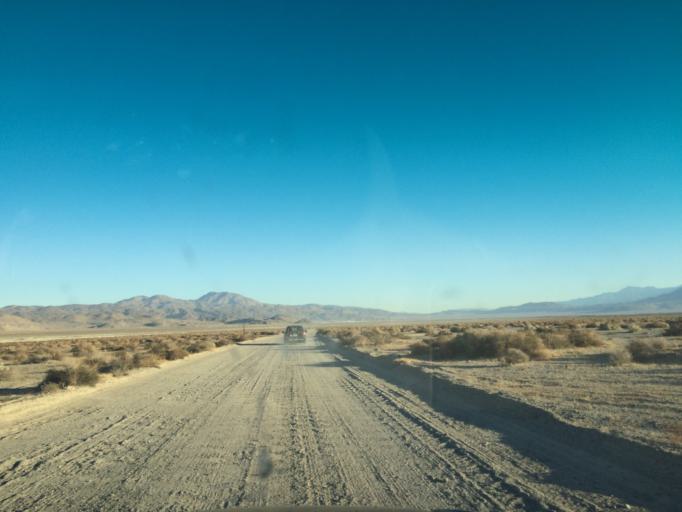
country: US
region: California
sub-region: San Bernardino County
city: Searles Valley
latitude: 35.6381
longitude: -117.3756
